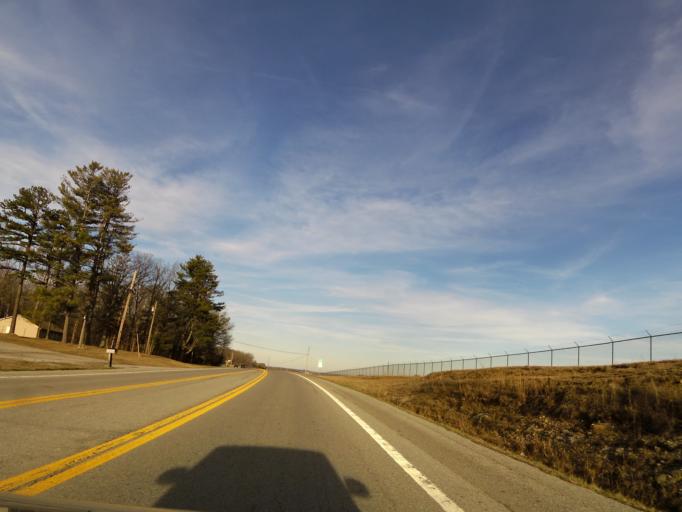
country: US
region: Tennessee
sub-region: Cumberland County
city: Crossville
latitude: 35.9501
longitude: -85.0945
